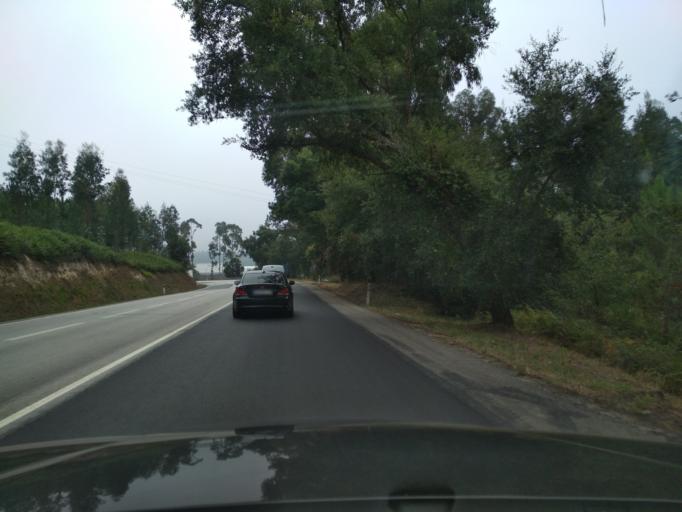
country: PT
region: Aveiro
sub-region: Mealhada
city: Pampilhosa do Botao
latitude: 40.3453
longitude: -8.4505
